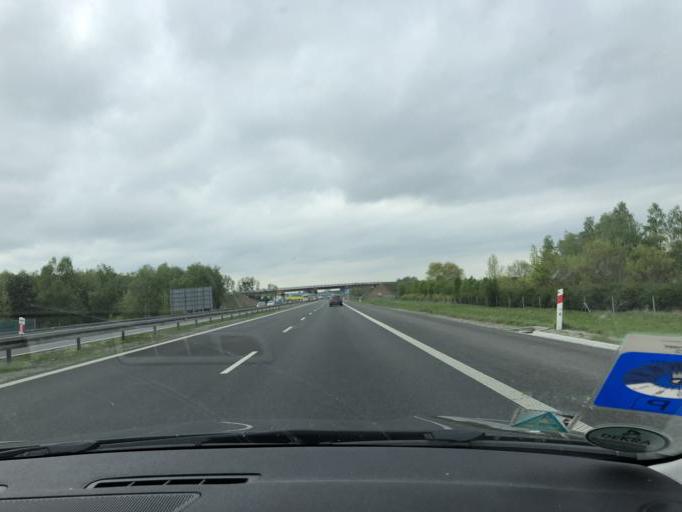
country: PL
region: Opole Voivodeship
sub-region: Powiat krapkowicki
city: Krapkowice
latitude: 50.5018
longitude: 17.9709
